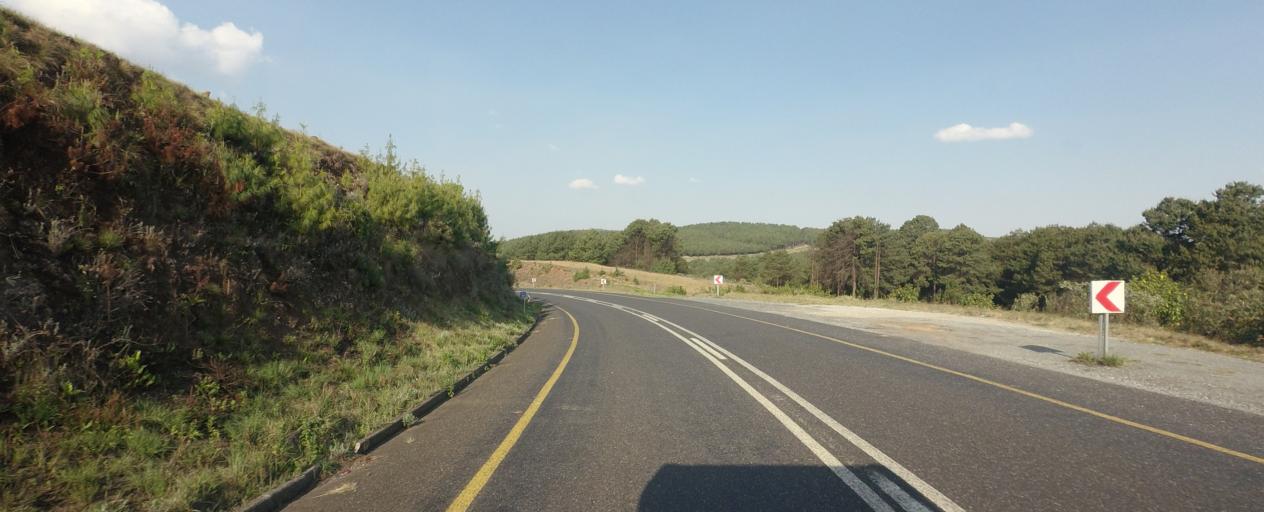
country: ZA
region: Mpumalanga
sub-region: Ehlanzeni District
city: Lydenburg
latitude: -25.1689
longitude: 30.6415
